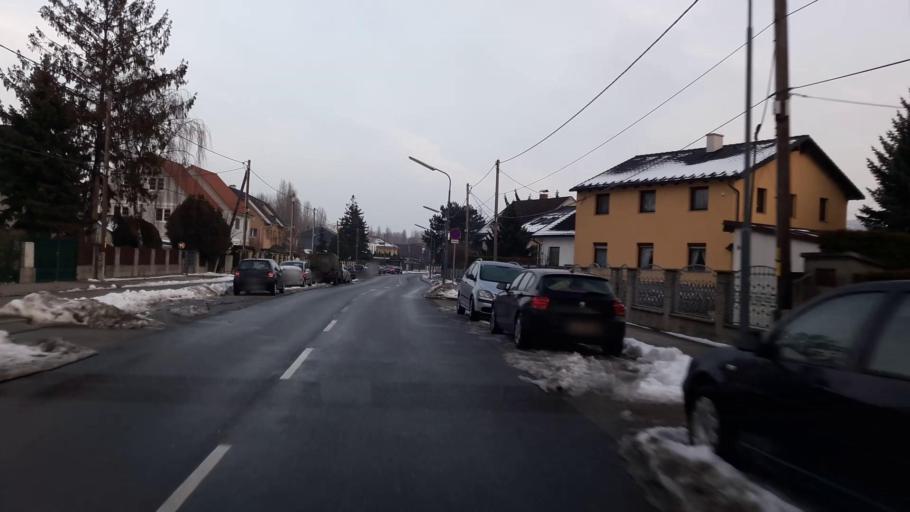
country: AT
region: Vienna
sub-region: Wien Stadt
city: Vienna
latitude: 48.2466
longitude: 16.4049
